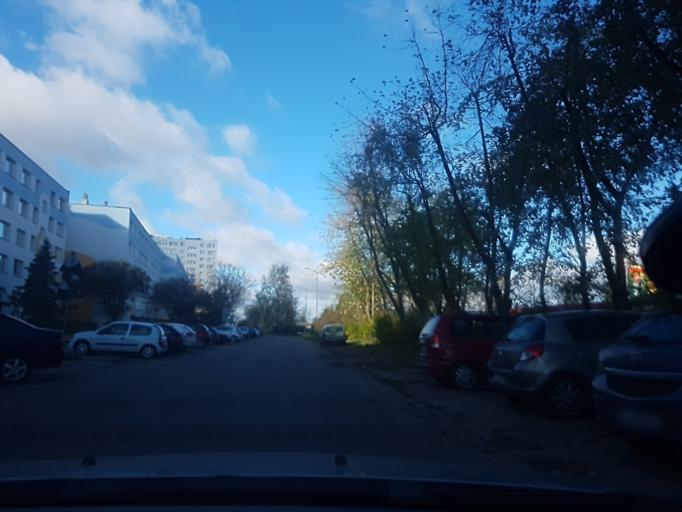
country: PL
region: Lodz Voivodeship
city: Lodz
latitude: 51.7608
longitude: 19.5333
